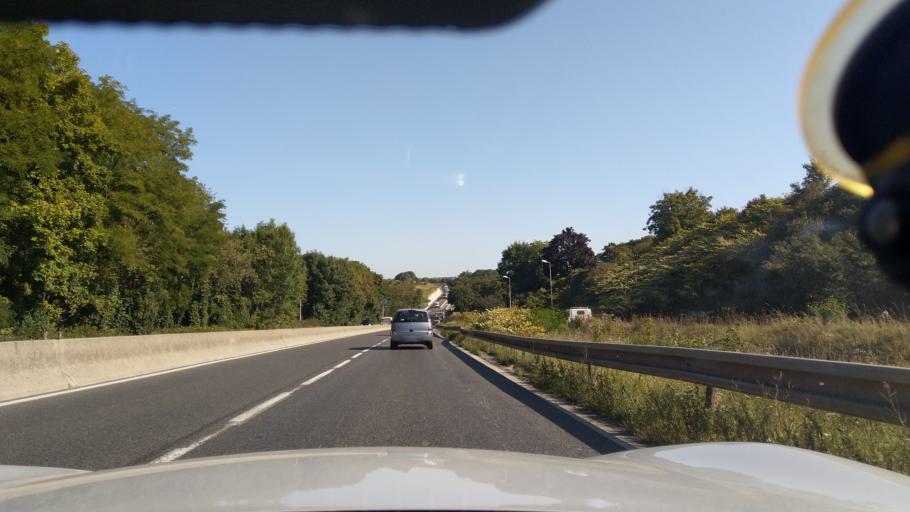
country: FR
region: Ile-de-France
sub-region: Departement du Val-d'Oise
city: Le Thillay
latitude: 48.9987
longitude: 2.4831
